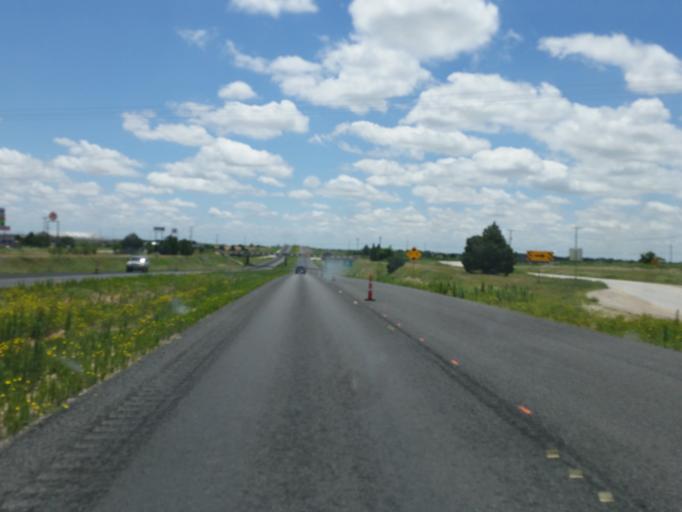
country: US
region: Texas
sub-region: Scurry County
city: Snyder
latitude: 32.7073
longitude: -100.8700
